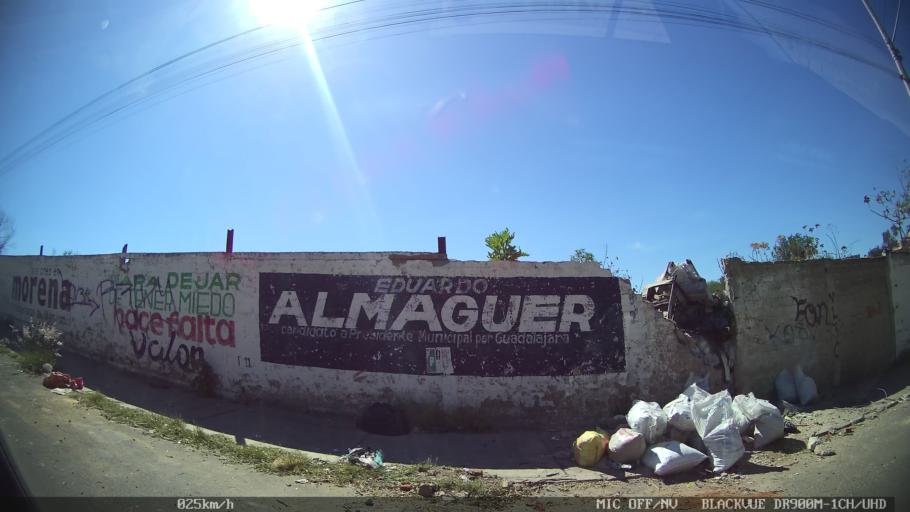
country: MX
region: Jalisco
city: Tlaquepaque
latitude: 20.7034
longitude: -103.2867
